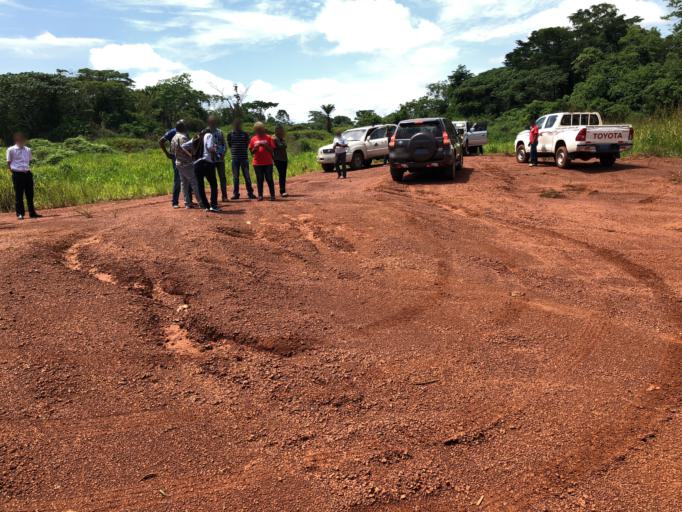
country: CD
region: Eastern Province
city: Kisangani
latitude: 0.4805
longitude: 25.5125
